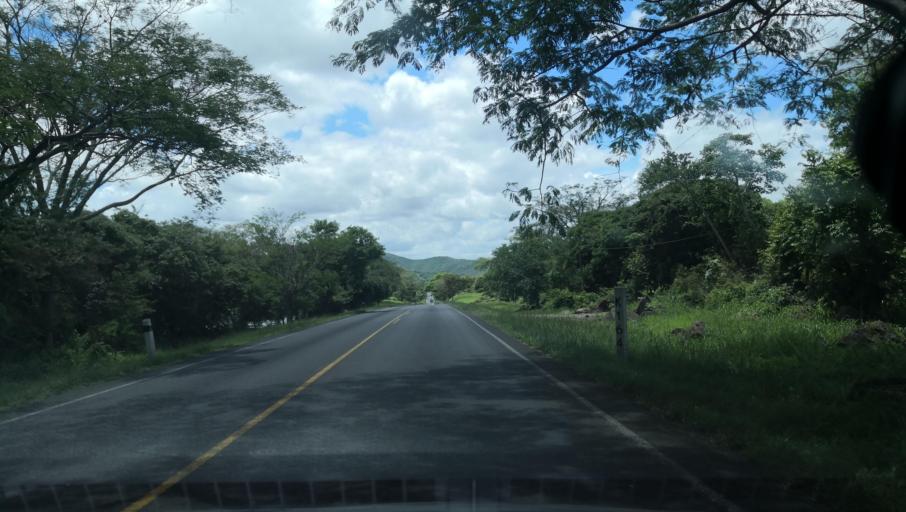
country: NI
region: Esteli
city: Esteli
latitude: 13.2263
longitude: -86.3787
